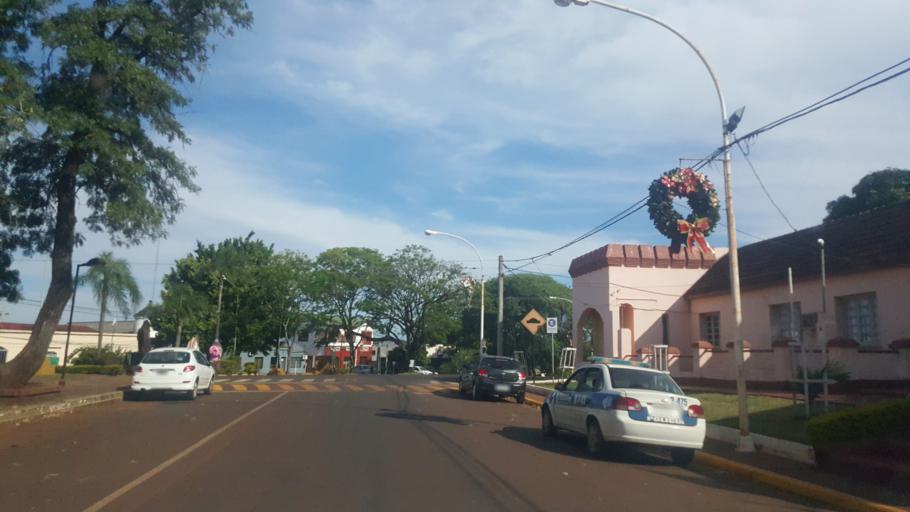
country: AR
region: Misiones
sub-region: Departamento de Leandro N. Alem
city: Leandro N. Alem
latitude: -27.6045
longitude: -55.3211
